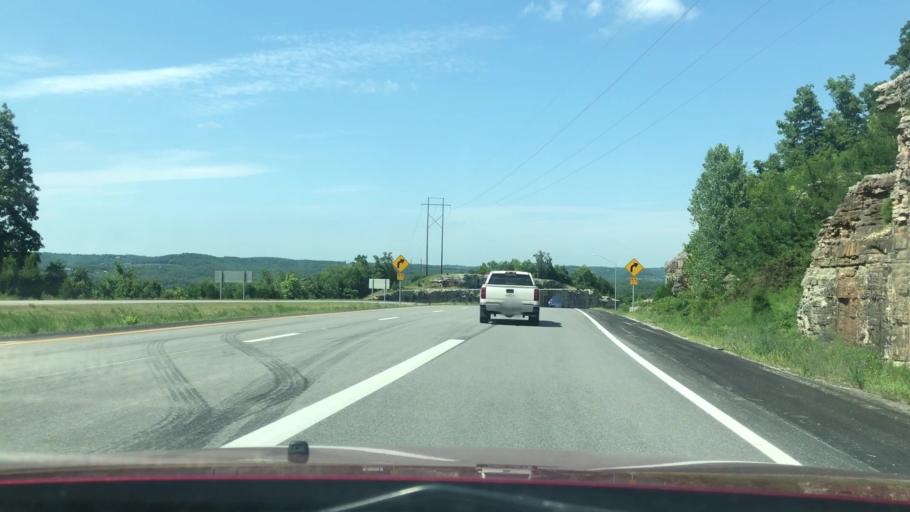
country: US
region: Missouri
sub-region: Taney County
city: Branson
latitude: 36.6794
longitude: -93.3161
